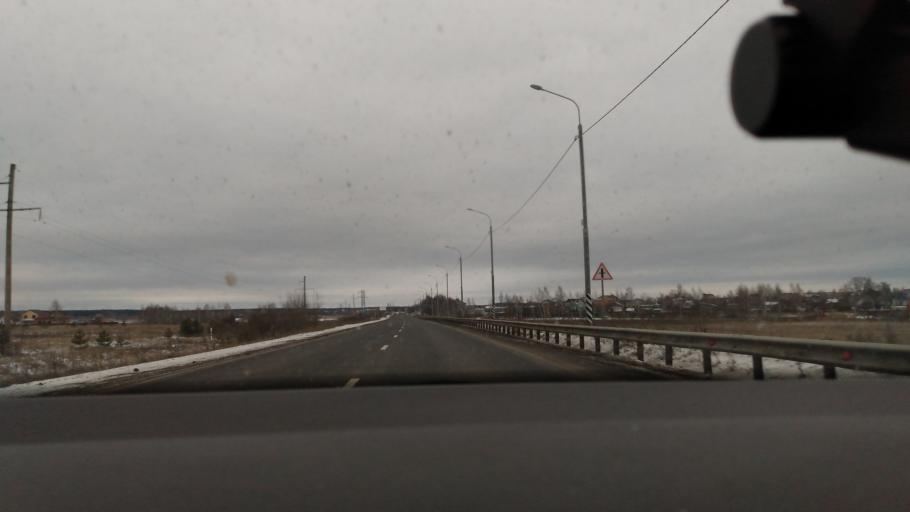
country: RU
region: Moskovskaya
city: Yegor'yevsk
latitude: 55.3962
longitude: 39.0663
